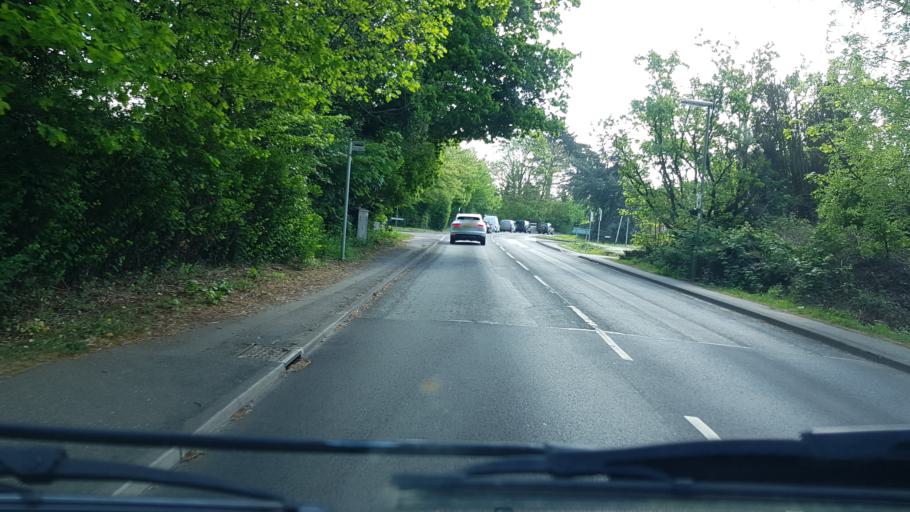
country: GB
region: England
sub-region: Surrey
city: Cobham
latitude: 51.3228
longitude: -0.3893
